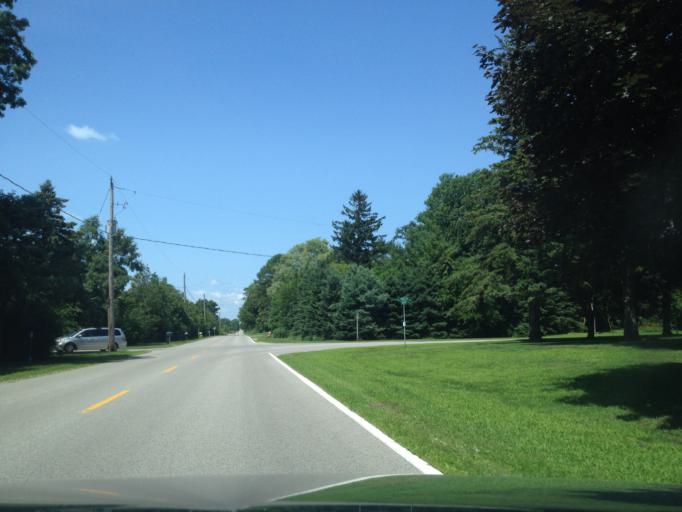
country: CA
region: Ontario
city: Aylmer
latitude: 42.6170
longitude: -80.7054
